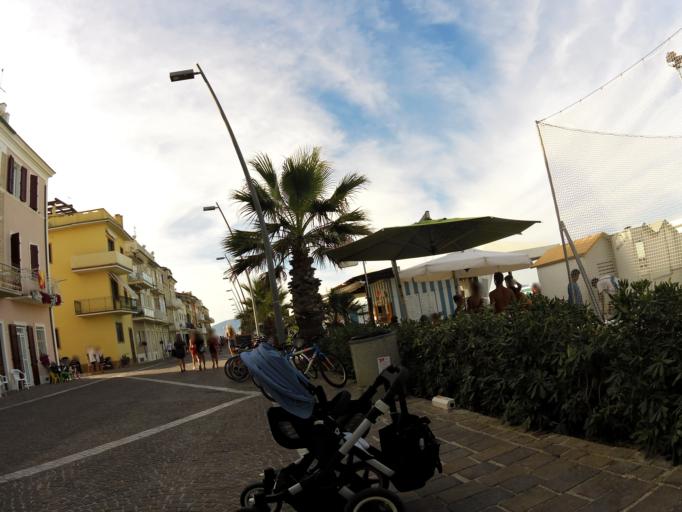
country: IT
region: The Marches
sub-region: Provincia di Macerata
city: Porto Recanati
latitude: 43.4372
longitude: 13.6629
